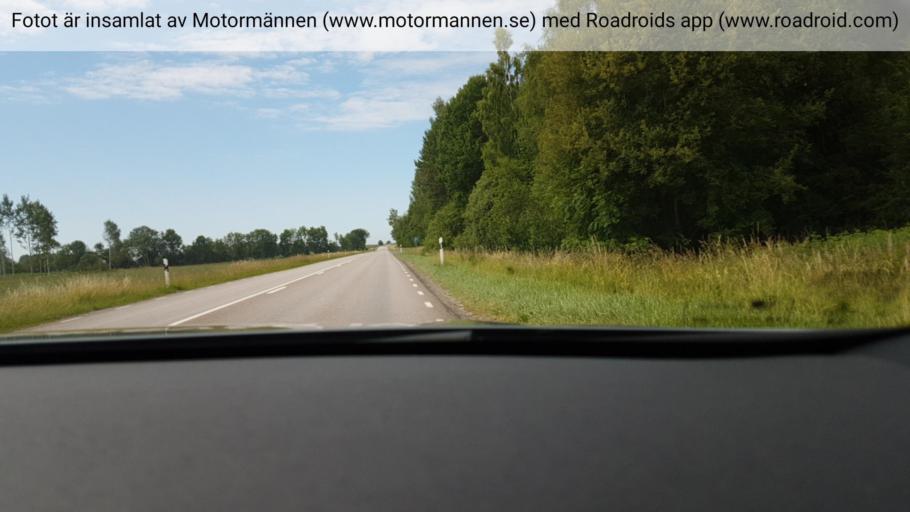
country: SE
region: Vaestra Goetaland
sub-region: Falkopings Kommun
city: Akarp
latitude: 58.2093
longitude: 13.6272
